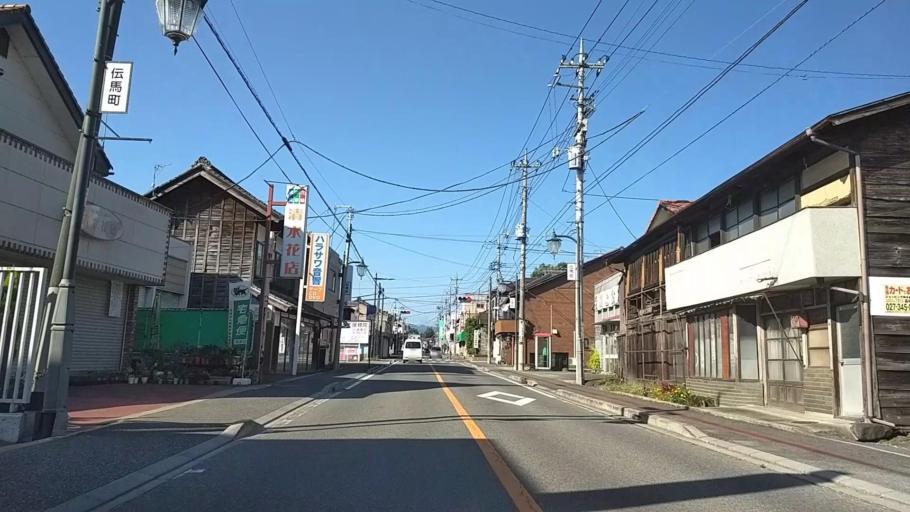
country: JP
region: Gunma
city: Annaka
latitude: 36.3294
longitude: 138.8997
